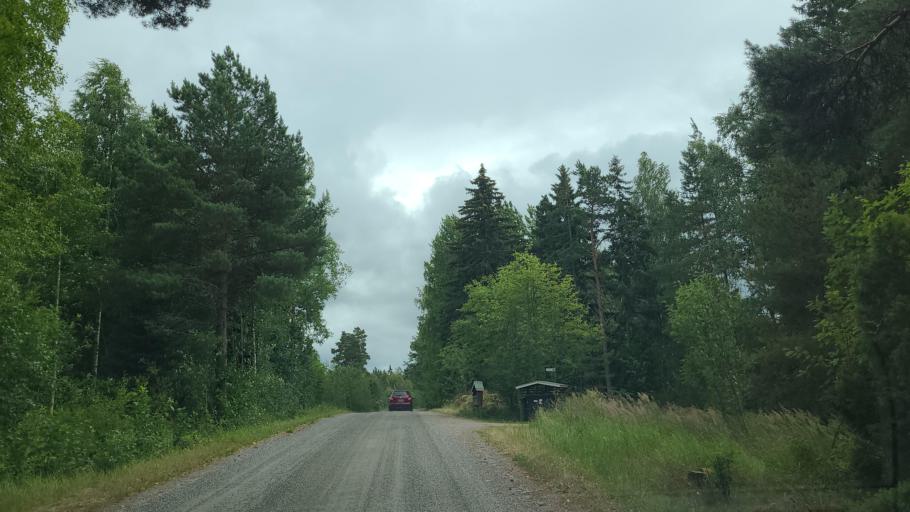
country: FI
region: Varsinais-Suomi
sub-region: Aboland-Turunmaa
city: Dragsfjaerd
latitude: 60.0901
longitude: 22.4160
